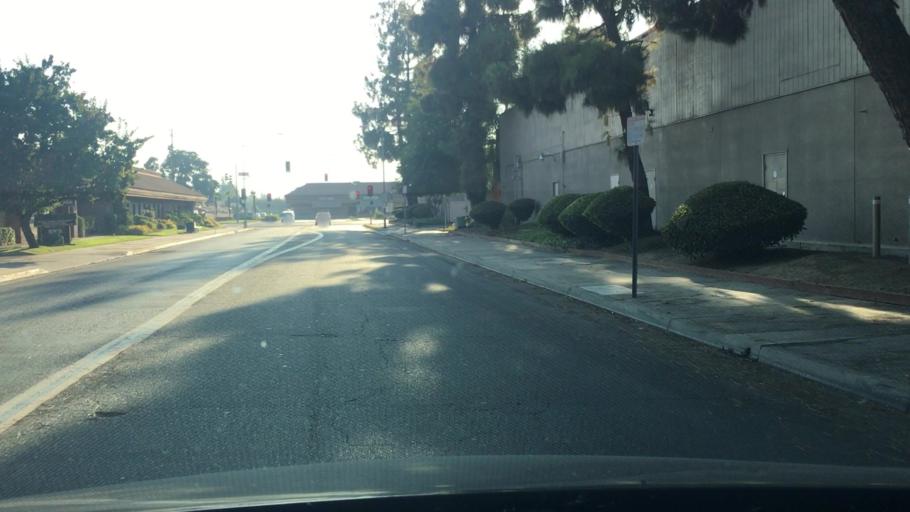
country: US
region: California
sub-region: Fresno County
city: Clovis
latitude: 36.8362
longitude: -119.7708
